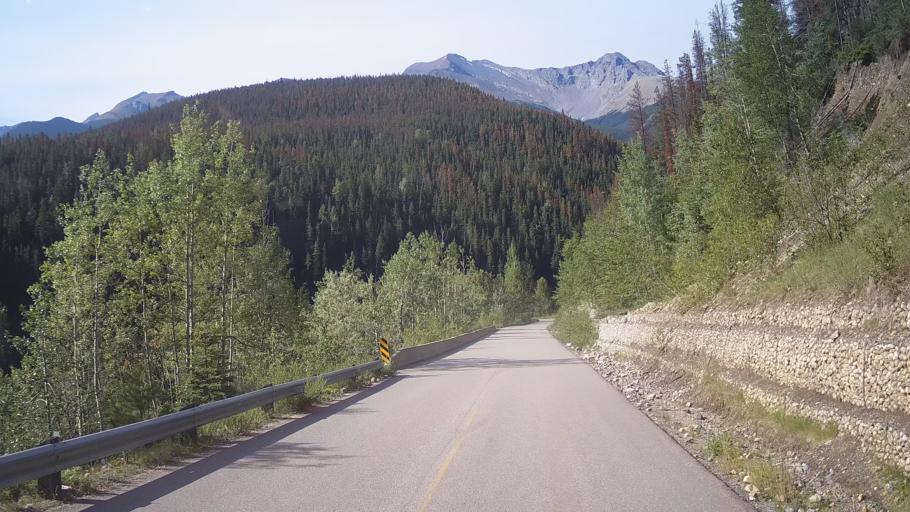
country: CA
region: Alberta
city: Hinton
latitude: 53.1778
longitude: -117.8390
